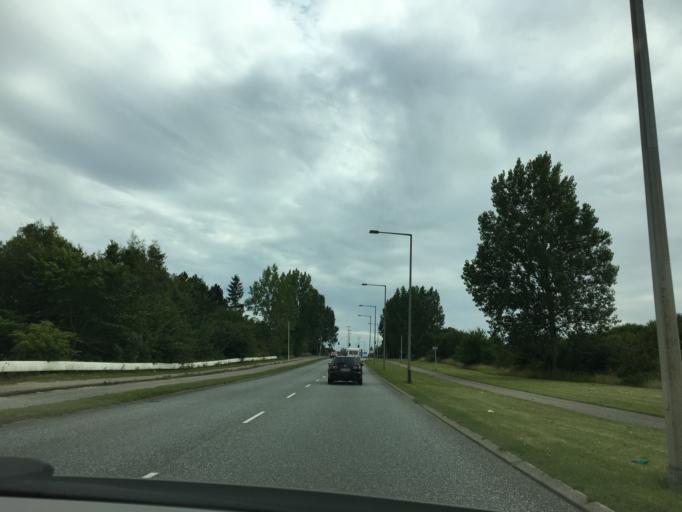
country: DK
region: South Denmark
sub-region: Fredericia Kommune
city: Fredericia
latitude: 55.5745
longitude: 9.7253
